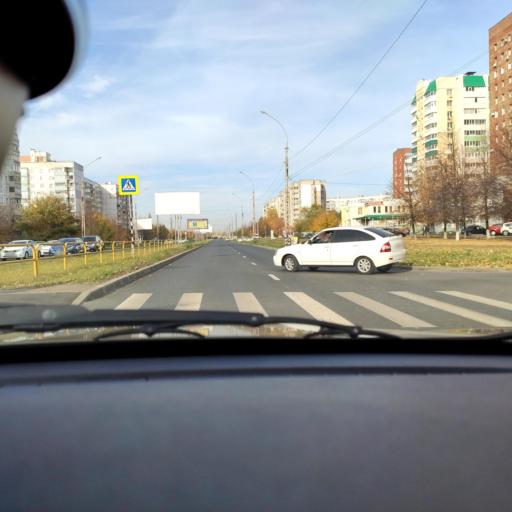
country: RU
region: Samara
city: Tol'yatti
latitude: 53.5446
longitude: 49.3314
